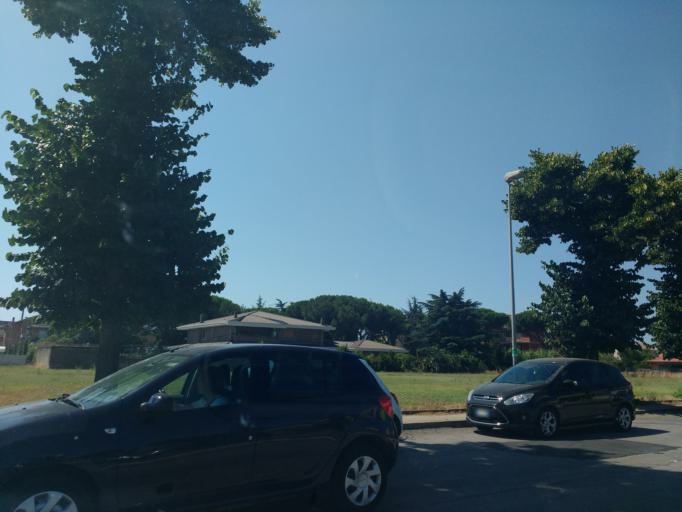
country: IT
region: Latium
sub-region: Citta metropolitana di Roma Capitale
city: Vitinia
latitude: 41.7791
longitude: 12.3691
